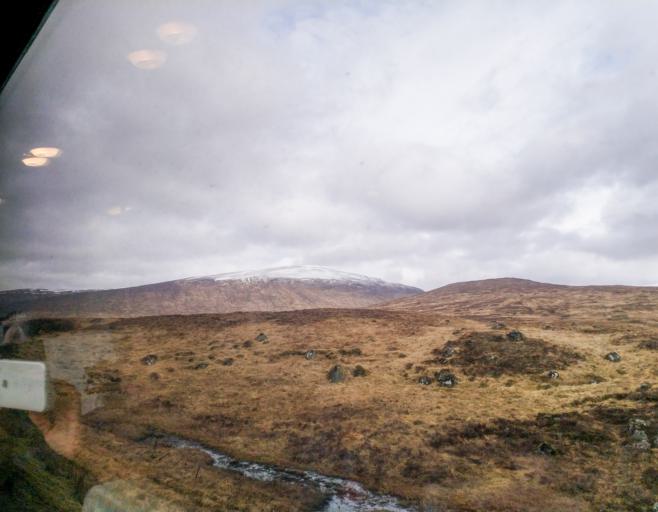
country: GB
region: Scotland
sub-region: Highland
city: Spean Bridge
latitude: 56.7420
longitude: -4.6670
